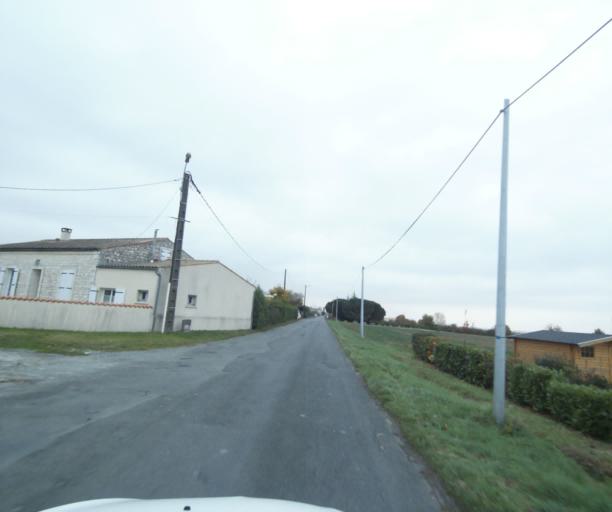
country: FR
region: Poitou-Charentes
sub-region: Departement de la Charente-Maritime
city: Les Gonds
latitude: 45.7398
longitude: -0.6034
